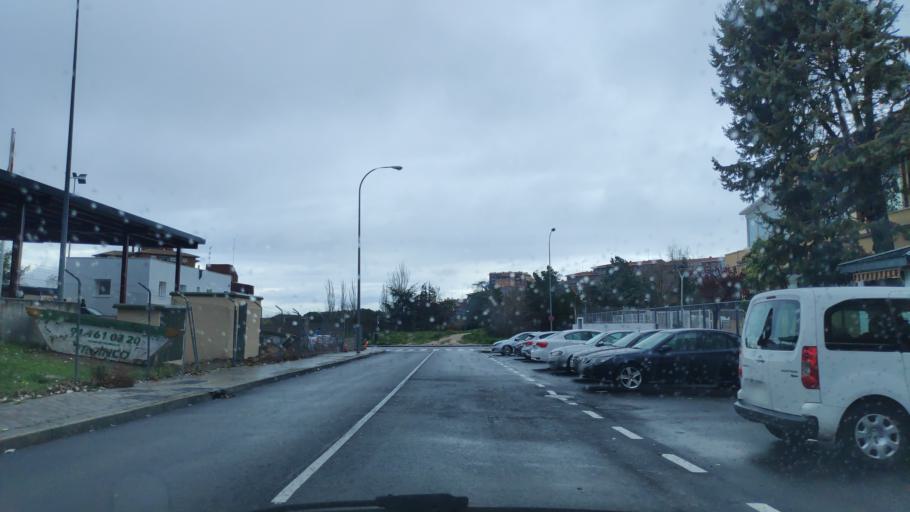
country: ES
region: Madrid
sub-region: Provincia de Madrid
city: Pinar de Chamartin
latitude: 40.4737
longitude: -3.6580
